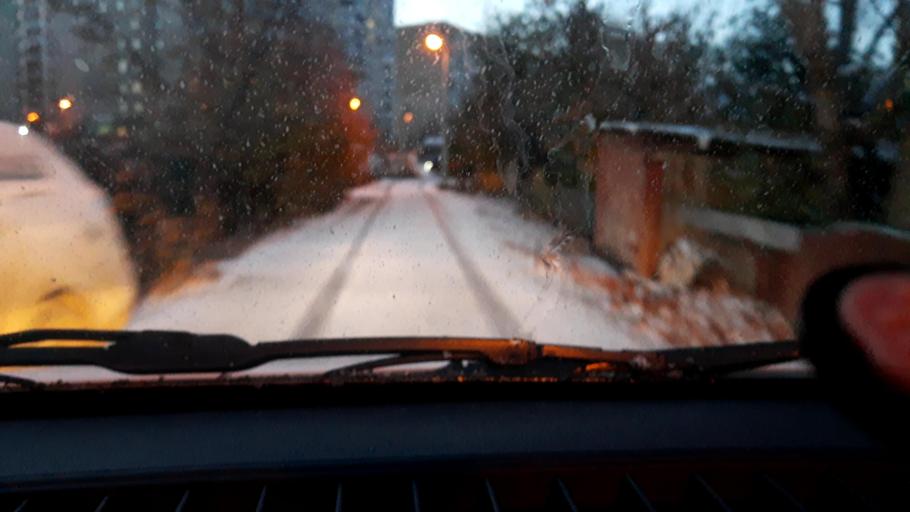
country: RU
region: Bashkortostan
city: Ufa
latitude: 54.7450
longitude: 55.9626
